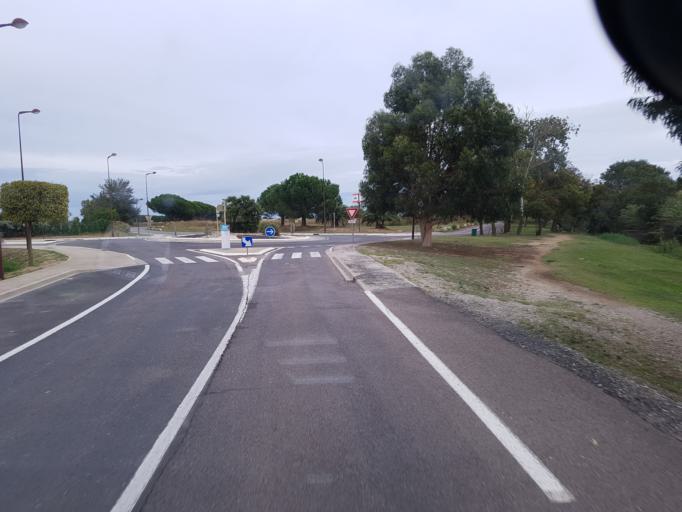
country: FR
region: Languedoc-Roussillon
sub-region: Departement des Pyrenees-Orientales
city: Torreilles
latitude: 42.7547
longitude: 3.0012
